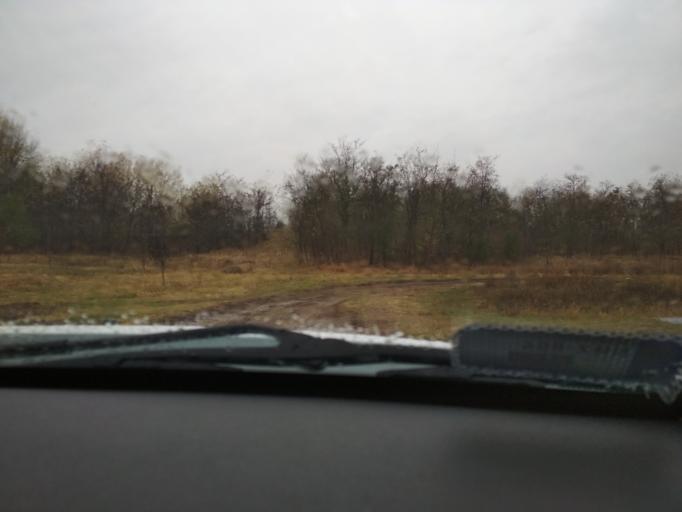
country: HU
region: Csongrad
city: Opusztaszer
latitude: 46.4360
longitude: 20.1339
